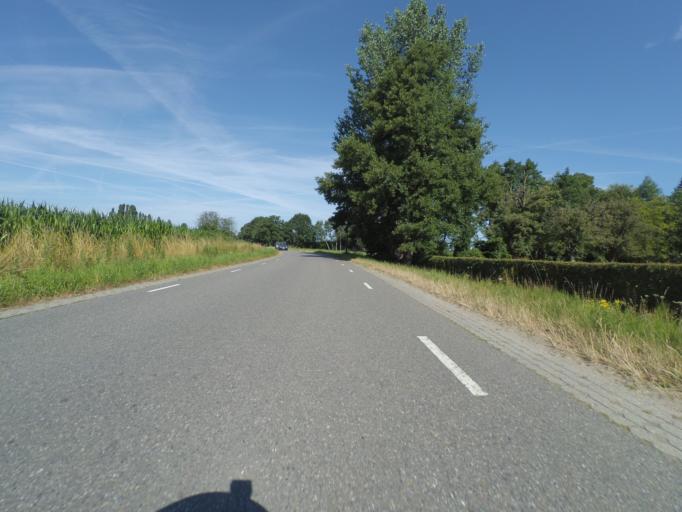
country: NL
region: Gelderland
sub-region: Gemeente Epe
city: Vaassen
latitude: 52.2552
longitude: 6.0210
